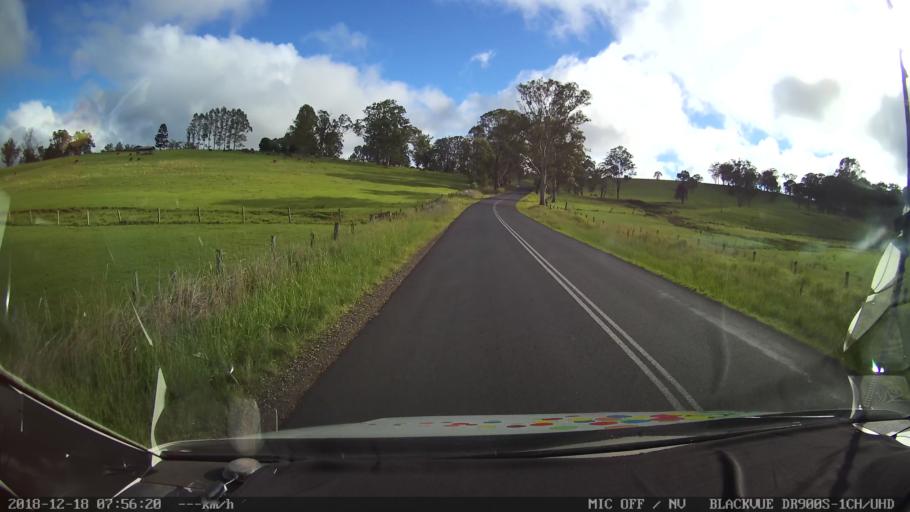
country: AU
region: New South Wales
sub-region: Kyogle
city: Kyogle
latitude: -28.3998
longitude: 152.6055
